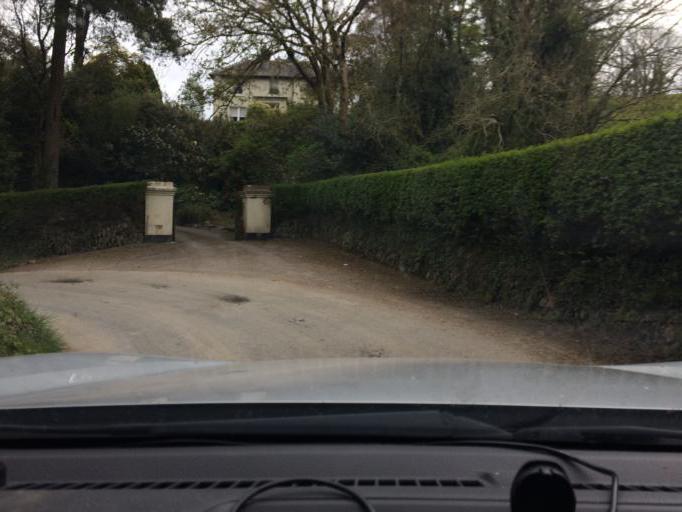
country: IE
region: Munster
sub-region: Waterford
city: Dungarvan
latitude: 52.0537
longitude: -7.6239
